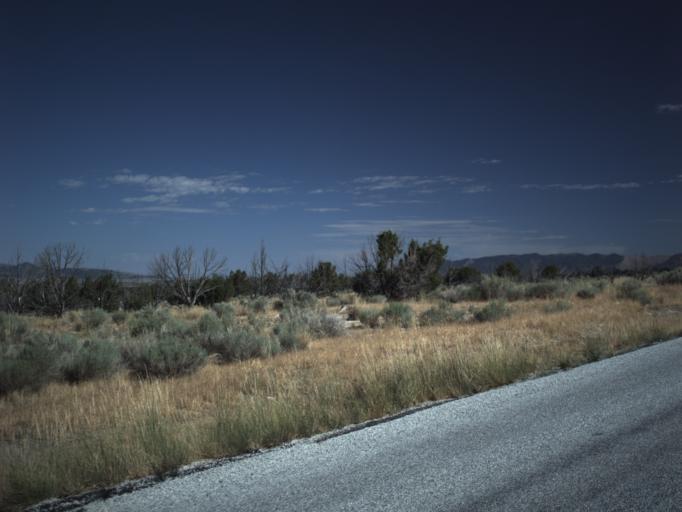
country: US
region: Utah
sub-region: Juab County
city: Mona
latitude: 39.7884
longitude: -112.1495
